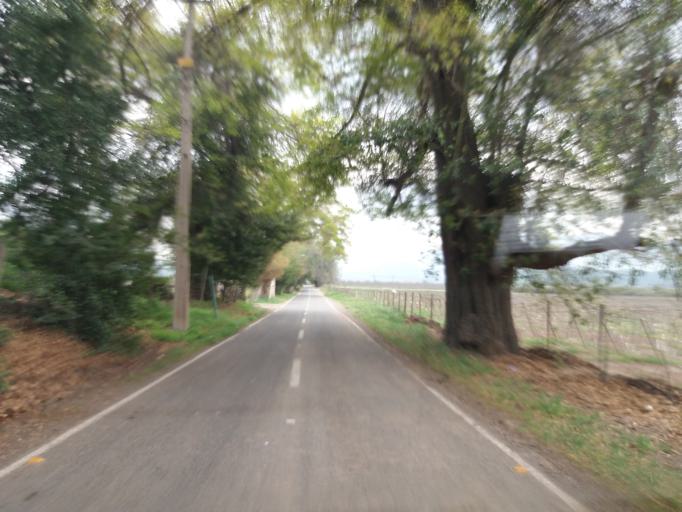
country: CL
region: Valparaiso
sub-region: Provincia de Quillota
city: Quillota
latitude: -32.8998
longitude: -71.1058
